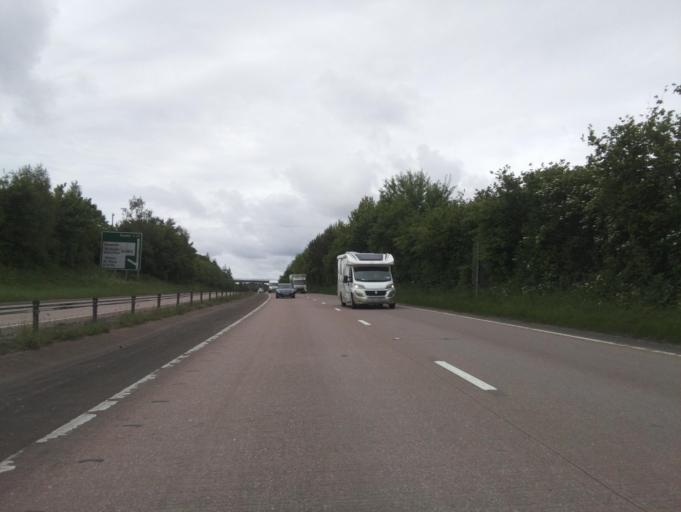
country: GB
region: England
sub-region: Devon
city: Ottery St Mary
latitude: 50.7573
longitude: -3.3276
